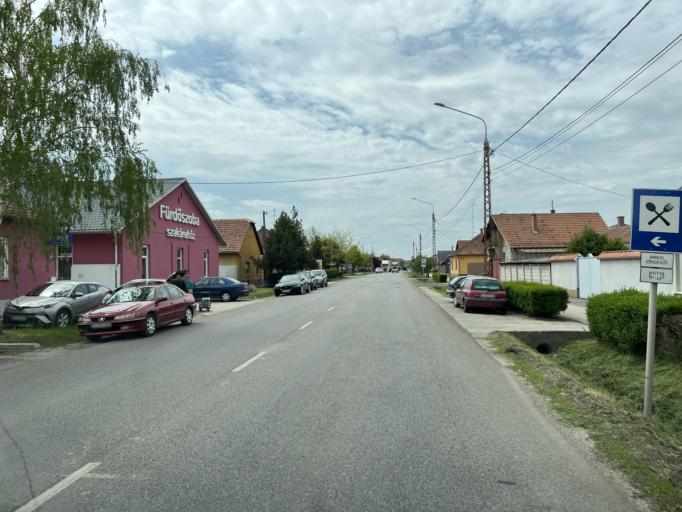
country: HU
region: Pest
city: Cegled
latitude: 47.1672
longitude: 19.8059
